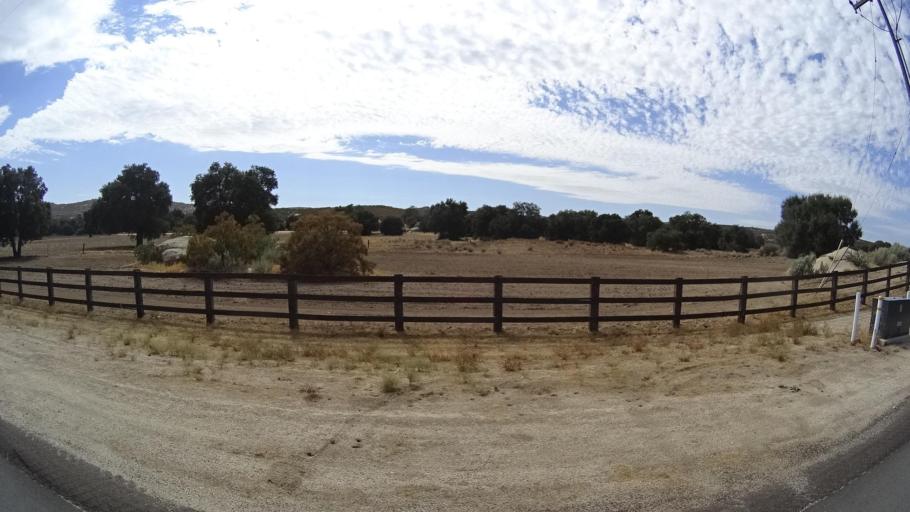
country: MX
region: Baja California
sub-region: Tecate
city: Cereso del Hongo
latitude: 32.6504
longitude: -116.2906
